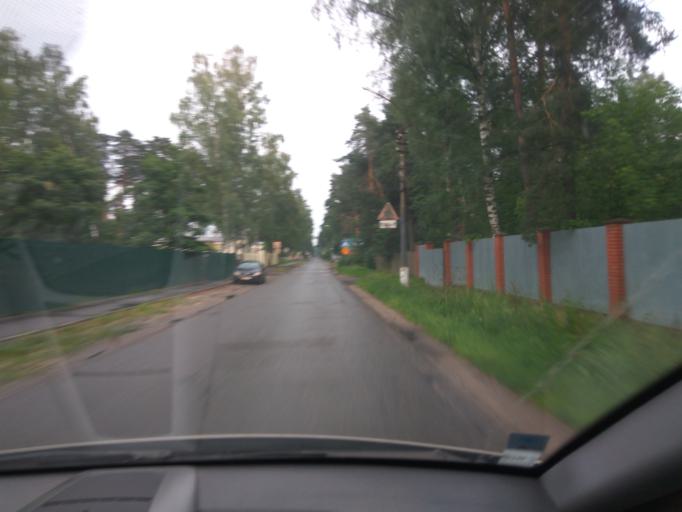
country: RU
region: Moskovskaya
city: Bykovo
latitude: 55.6322
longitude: 38.0631
